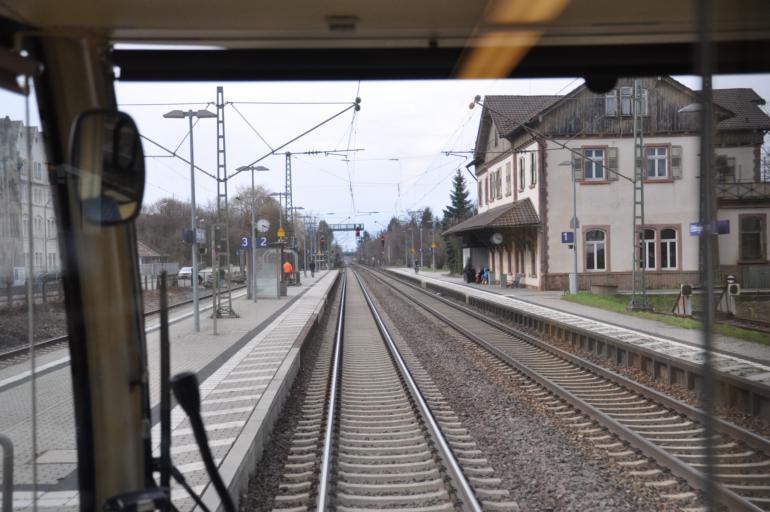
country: DE
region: Baden-Wuerttemberg
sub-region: Karlsruhe Region
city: Ettlingen
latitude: 48.9464
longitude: 8.3877
